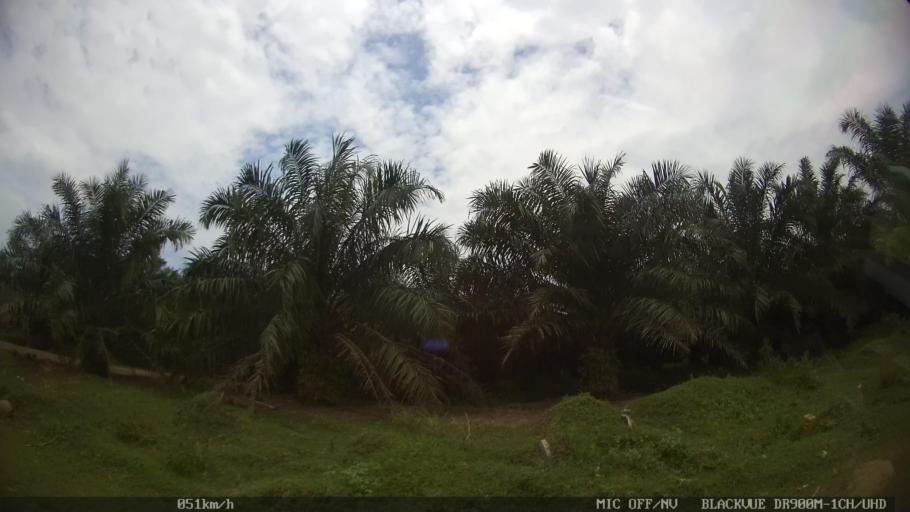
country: ID
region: North Sumatra
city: Sunggal
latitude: 3.6331
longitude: 98.5837
